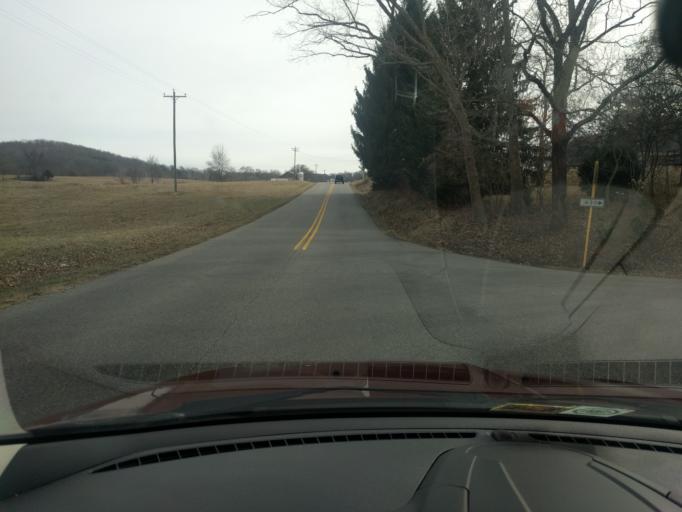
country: US
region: Virginia
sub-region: Augusta County
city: Fishersville
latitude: 38.0841
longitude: -78.9753
